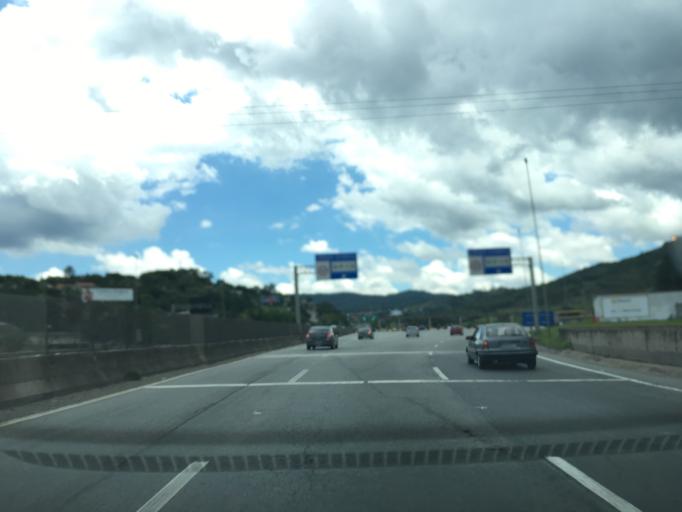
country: BR
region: Sao Paulo
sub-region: Mairipora
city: Mairipora
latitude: -23.3277
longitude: -46.5782
